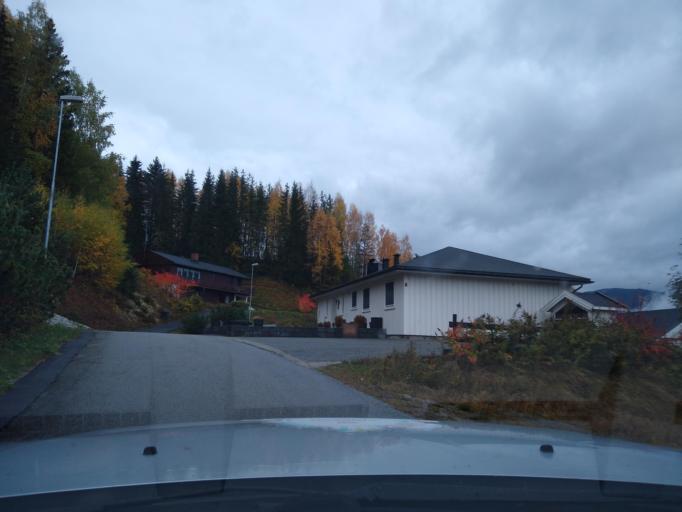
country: NO
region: Oppland
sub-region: Ringebu
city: Ringebu
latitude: 61.4579
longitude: 10.2008
